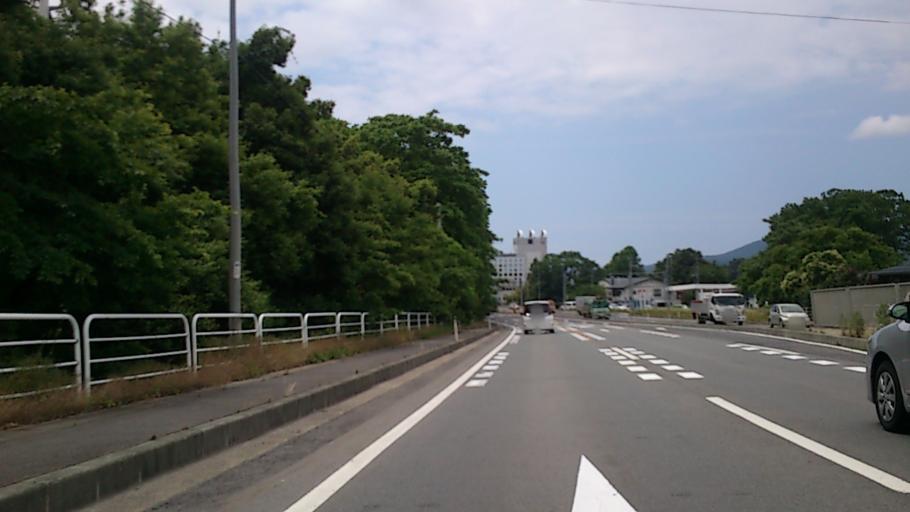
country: JP
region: Yamagata
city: Kaminoyama
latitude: 38.1765
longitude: 140.3071
